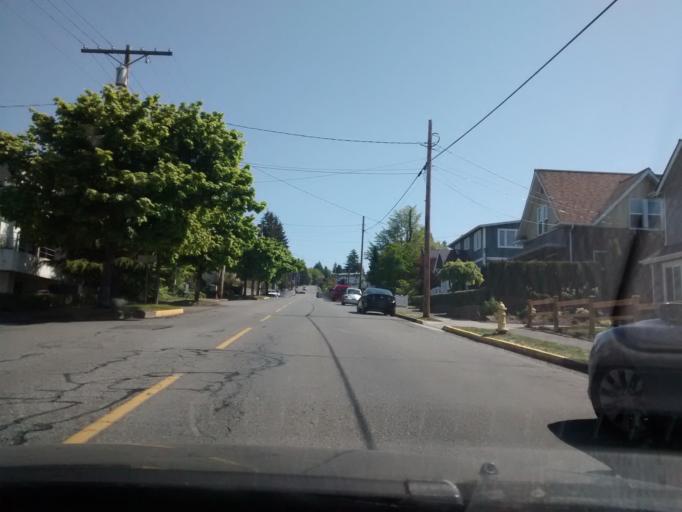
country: US
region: Washington
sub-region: Snohomish County
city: Edmonds
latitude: 47.8097
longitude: -122.3737
